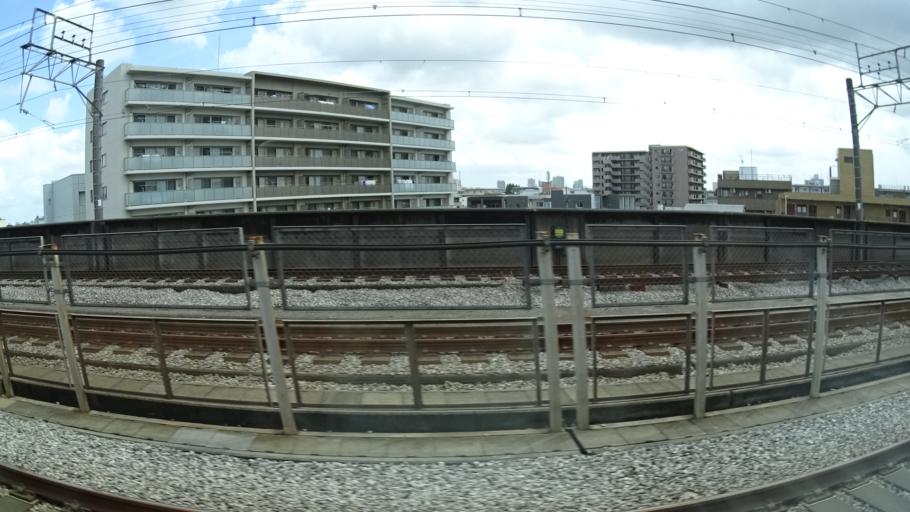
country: JP
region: Saitama
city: Shimotoda
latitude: 35.7974
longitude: 139.6859
